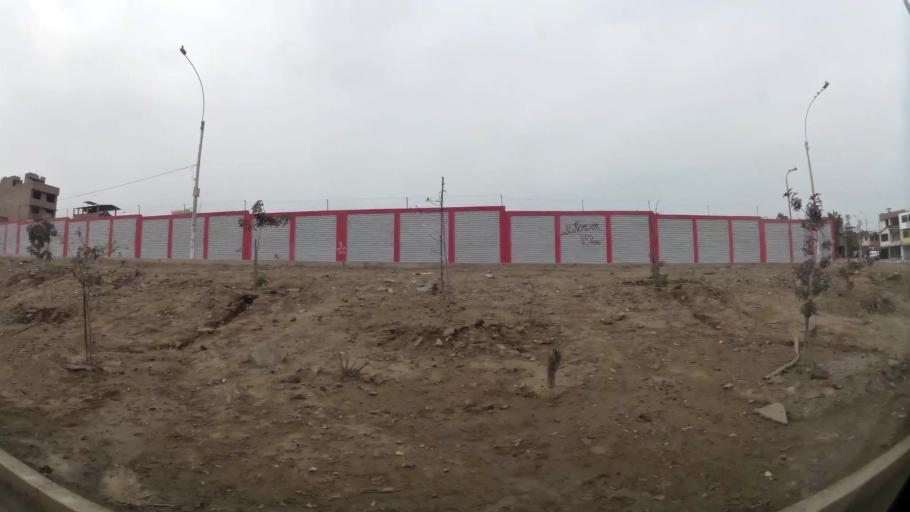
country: PE
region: Lima
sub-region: Lima
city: Surco
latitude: -12.2205
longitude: -76.9495
